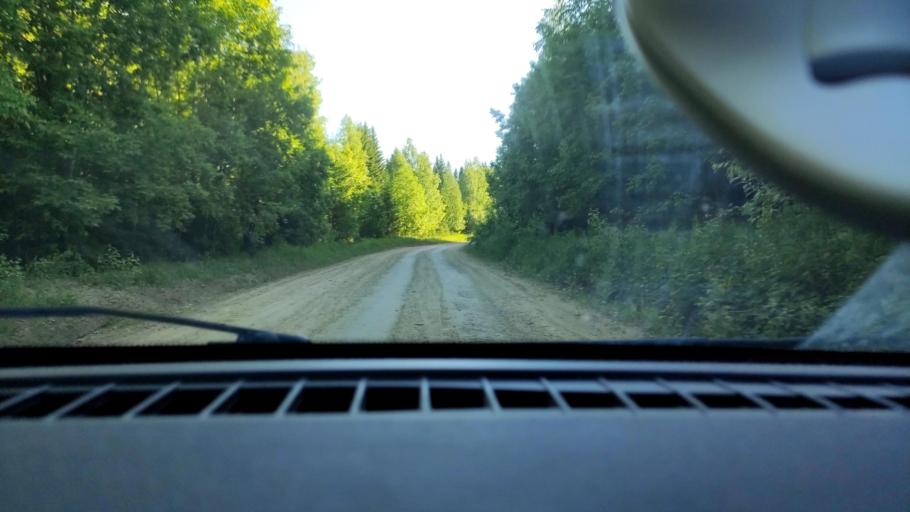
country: RU
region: Perm
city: Novyye Lyady
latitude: 58.1824
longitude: 56.5732
